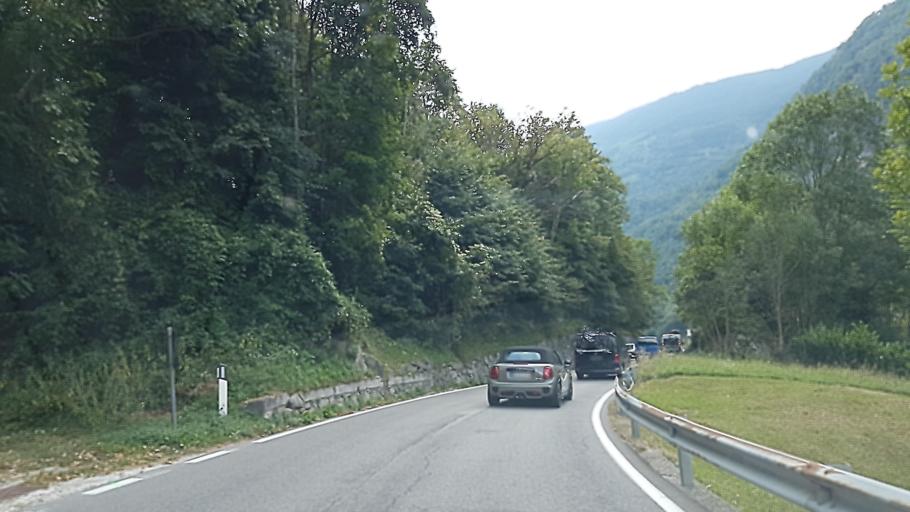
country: IT
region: Lombardy
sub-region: Provincia di Sondrio
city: San Giacomo Filippo
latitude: 46.3432
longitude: 9.3710
